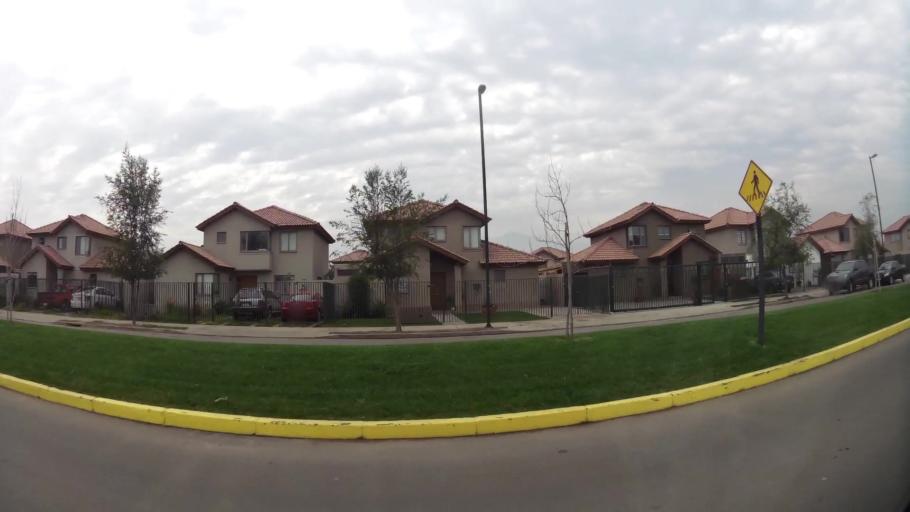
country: CL
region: Santiago Metropolitan
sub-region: Provincia de Chacabuco
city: Chicureo Abajo
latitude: -33.2179
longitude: -70.6737
